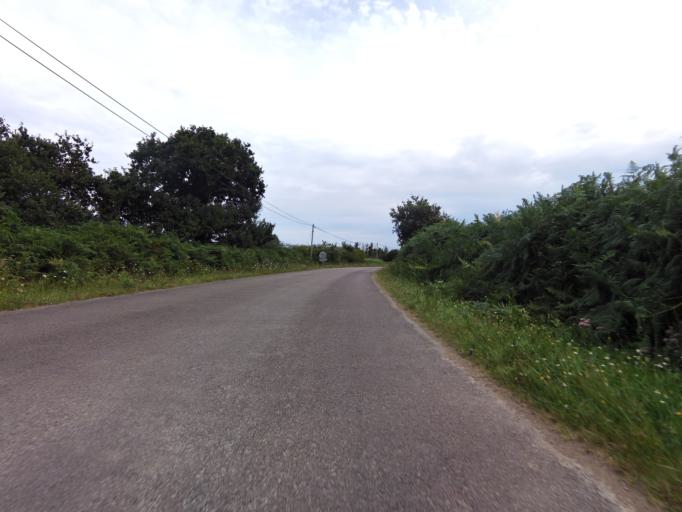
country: FR
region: Brittany
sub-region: Departement du Finistere
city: Poullan-sur-Mer
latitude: 48.0876
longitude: -4.4642
